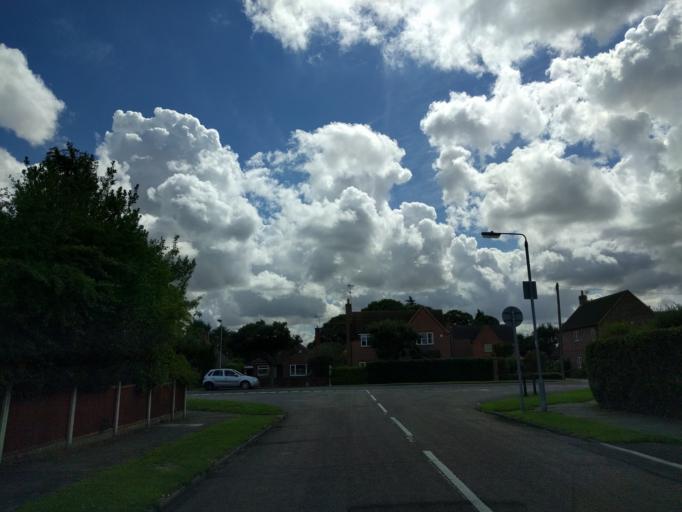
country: GB
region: England
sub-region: Nottinghamshire
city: Newark on Trent
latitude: 53.0620
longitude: -0.8239
